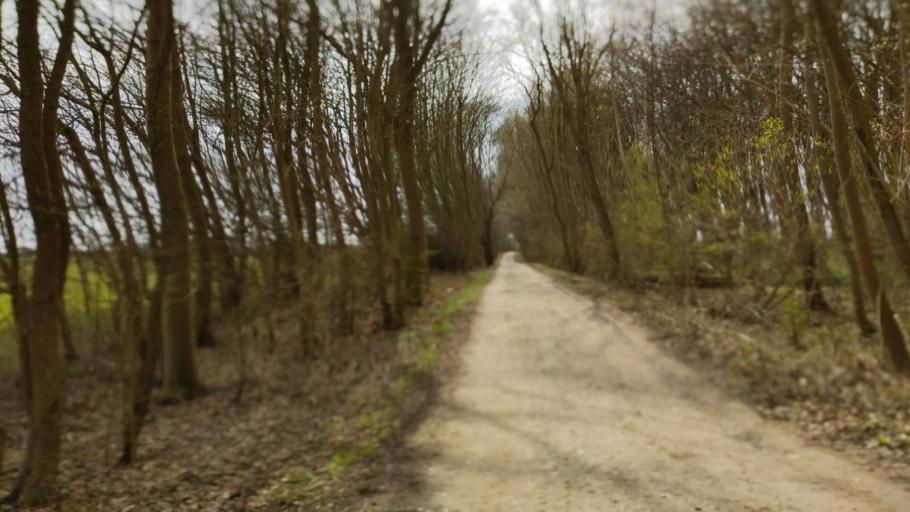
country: DE
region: Mecklenburg-Vorpommern
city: Dassow
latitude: 53.9685
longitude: 10.9441
